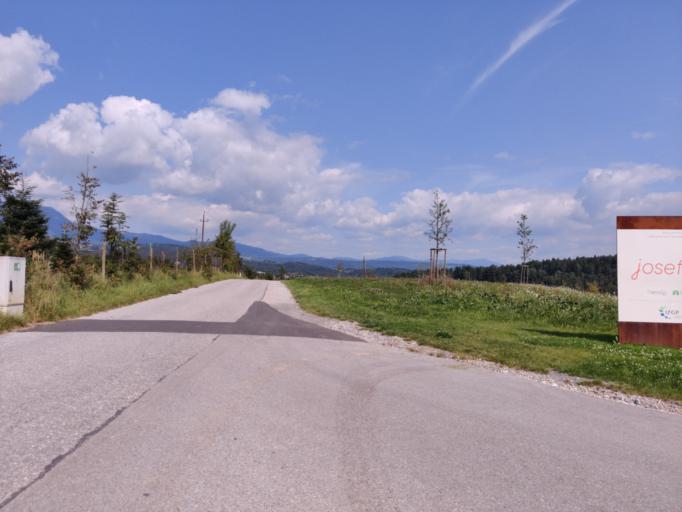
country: AT
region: Styria
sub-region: Graz Stadt
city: Mariatrost
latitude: 47.1267
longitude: 15.4983
